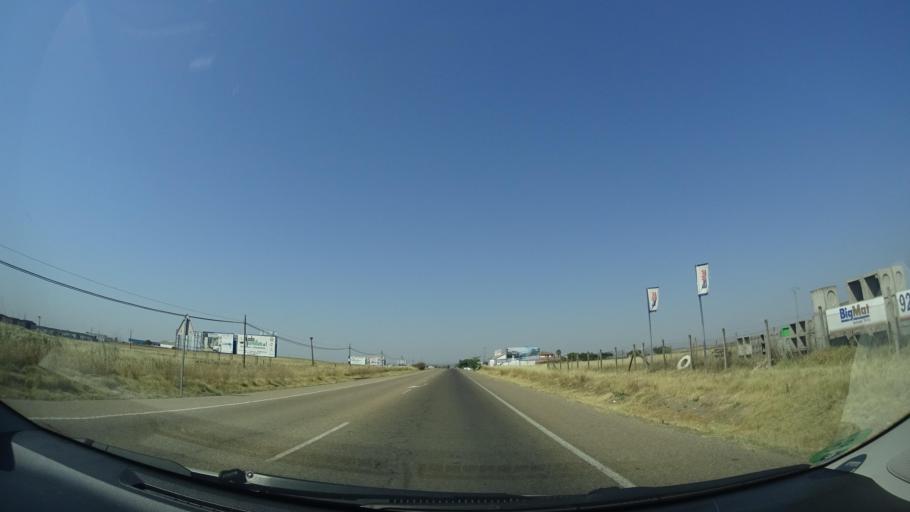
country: ES
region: Extremadura
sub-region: Provincia de Caceres
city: Miajadas
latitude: 39.1422
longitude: -5.9279
